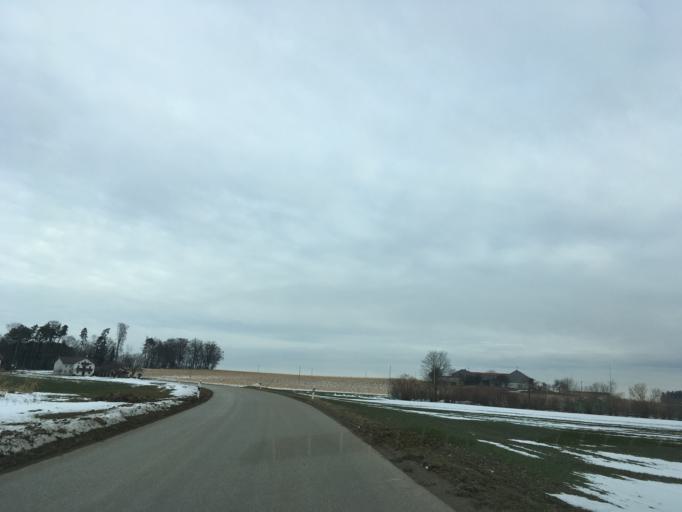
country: DE
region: Bavaria
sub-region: Upper Bavaria
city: Jettenbach
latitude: 48.1280
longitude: 12.3850
